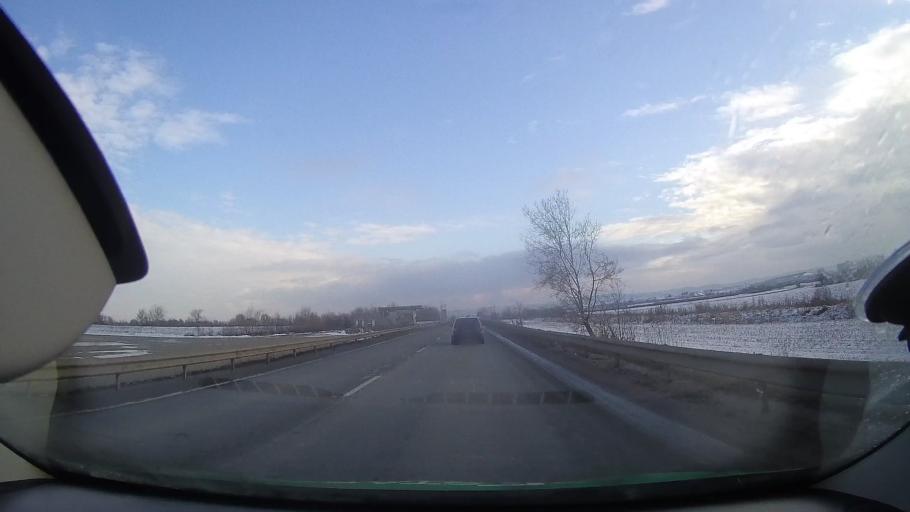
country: RO
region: Mures
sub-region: Comuna Iernut
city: Iernut
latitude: 46.4472
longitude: 24.2457
